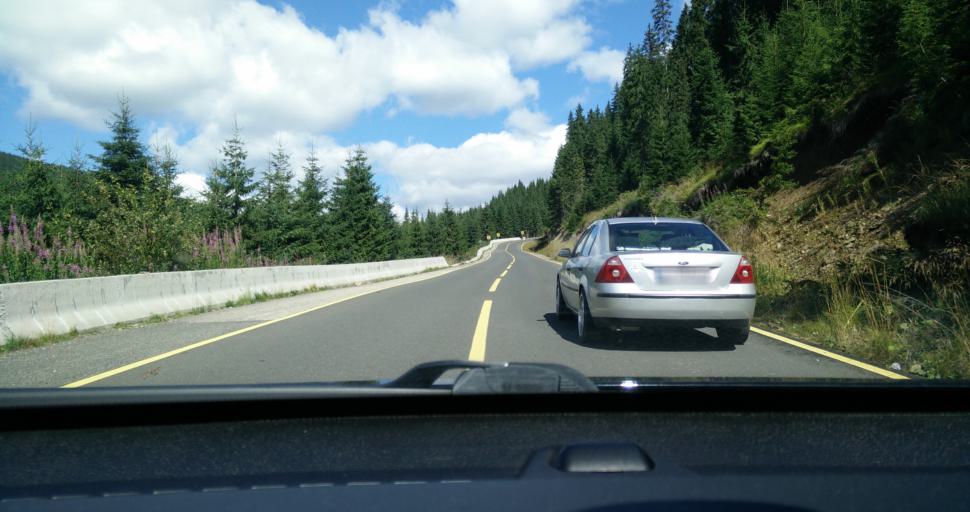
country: RO
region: Hunedoara
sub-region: Oras Petrila
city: Petrila
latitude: 45.4471
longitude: 23.6214
